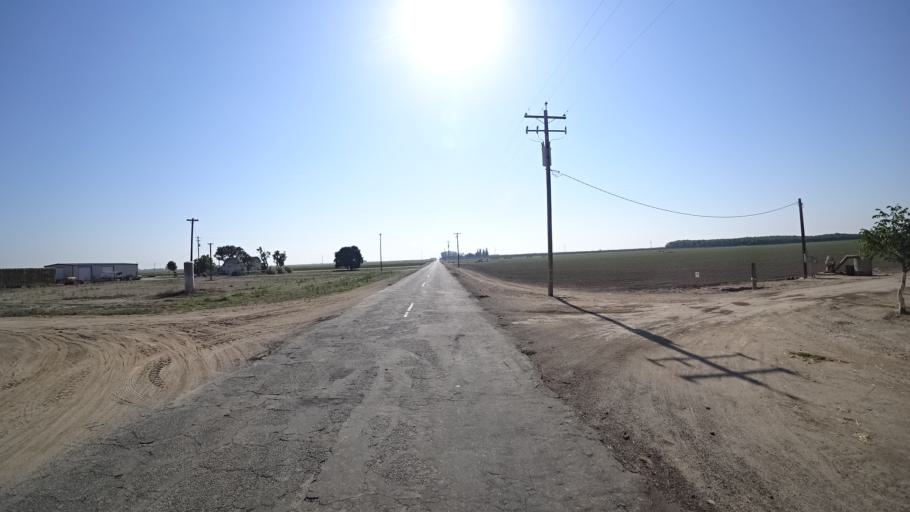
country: US
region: California
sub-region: Kings County
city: Lucerne
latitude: 36.3865
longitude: -119.6014
